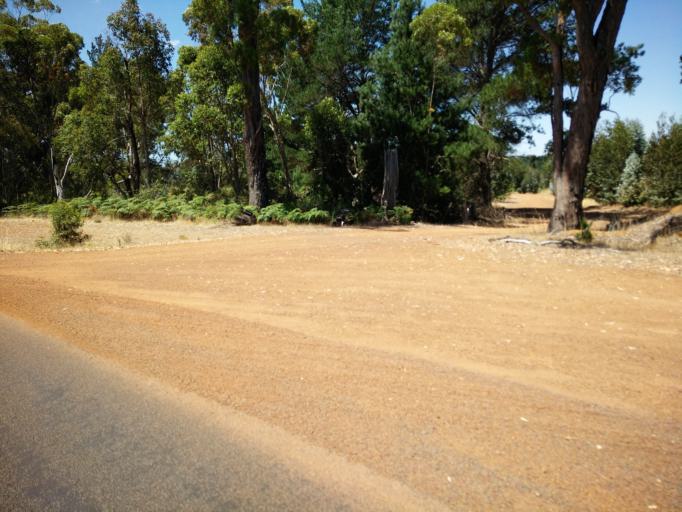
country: AU
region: Western Australia
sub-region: Bridgetown-Greenbushes
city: Bridgetown
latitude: -33.9046
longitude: 116.0381
